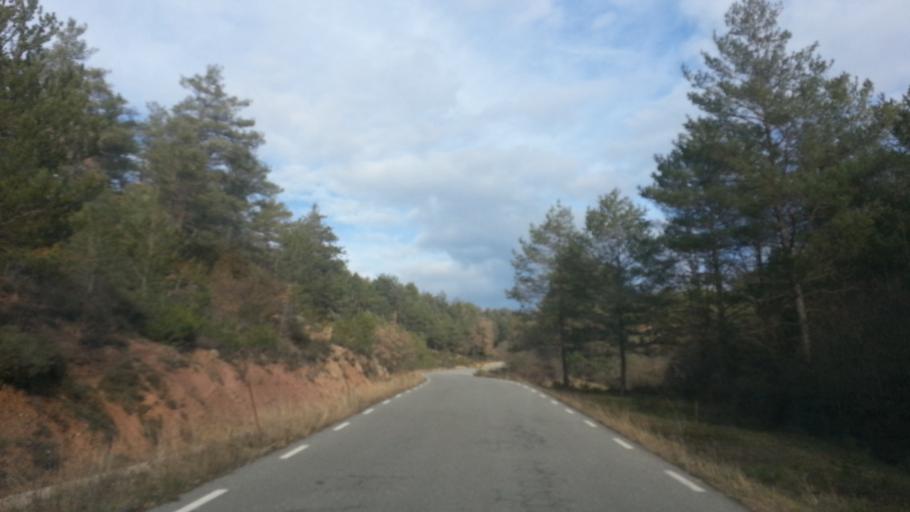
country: ES
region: Catalonia
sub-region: Provincia de Barcelona
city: Borreda
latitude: 42.1147
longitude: 2.0298
